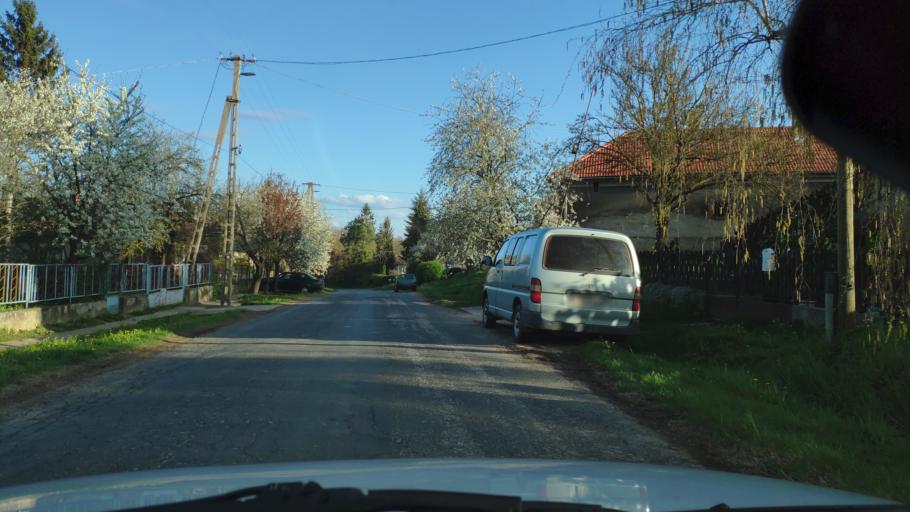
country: HU
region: Zala
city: Zalakomar
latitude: 46.4416
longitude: 17.1212
